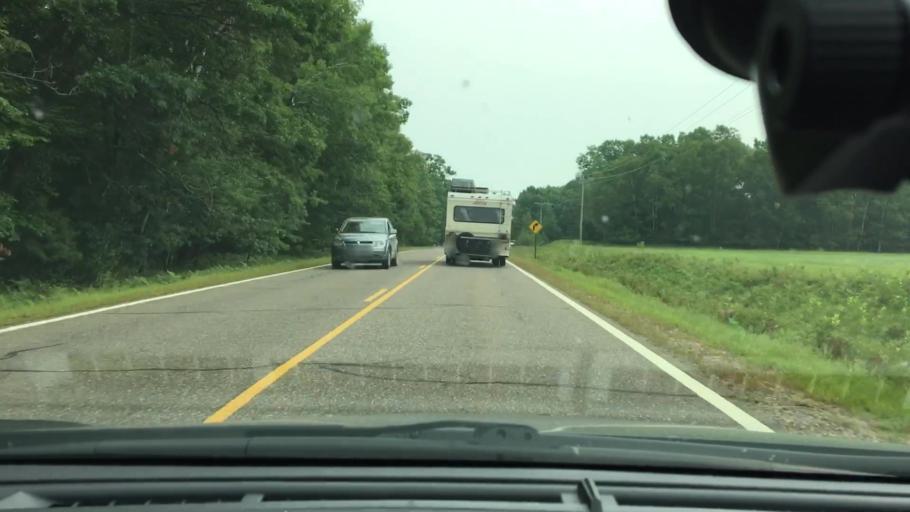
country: US
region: Minnesota
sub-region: Aitkin County
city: Aitkin
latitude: 46.4045
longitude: -93.7826
